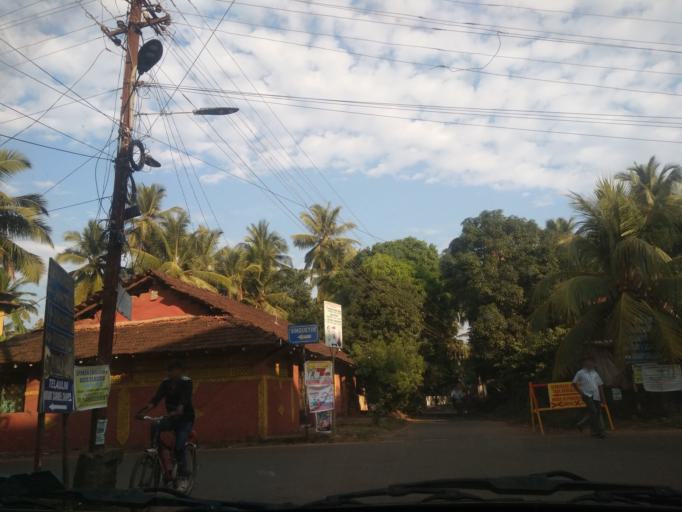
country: IN
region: Goa
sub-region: South Goa
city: Madgaon
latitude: 15.2532
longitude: 73.9561
